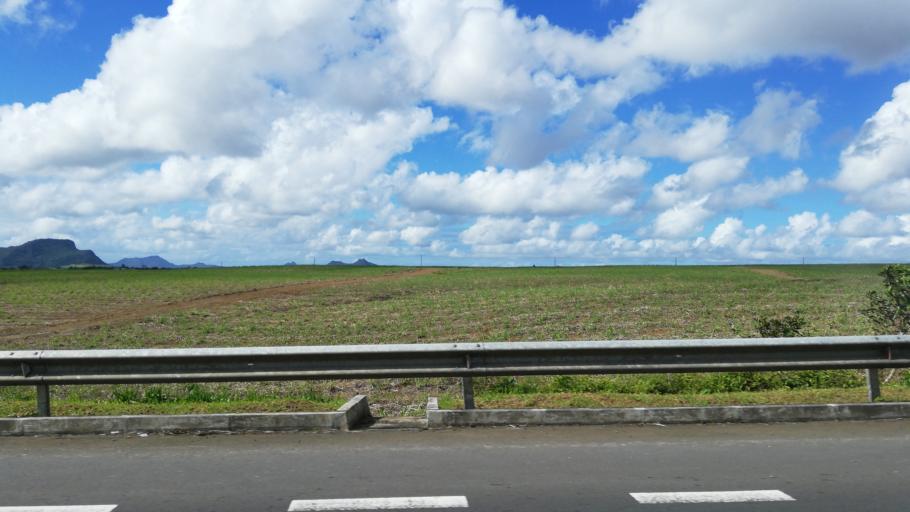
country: MU
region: Moka
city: Providence
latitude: -20.2391
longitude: 57.6224
